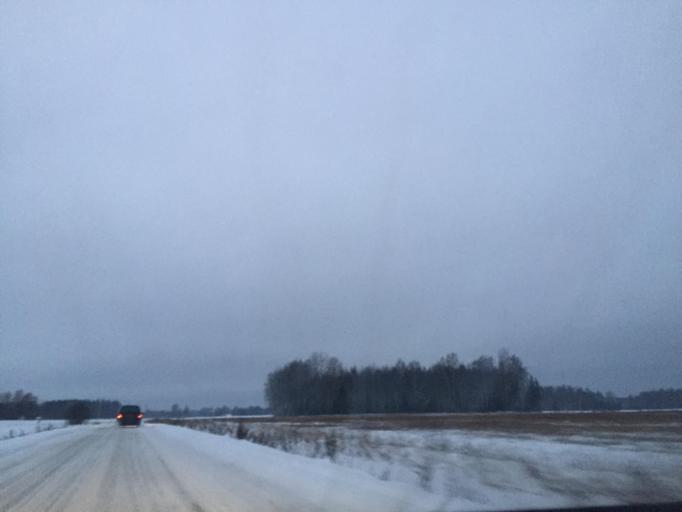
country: LV
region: Raunas
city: Rauna
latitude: 57.4195
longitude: 25.5681
